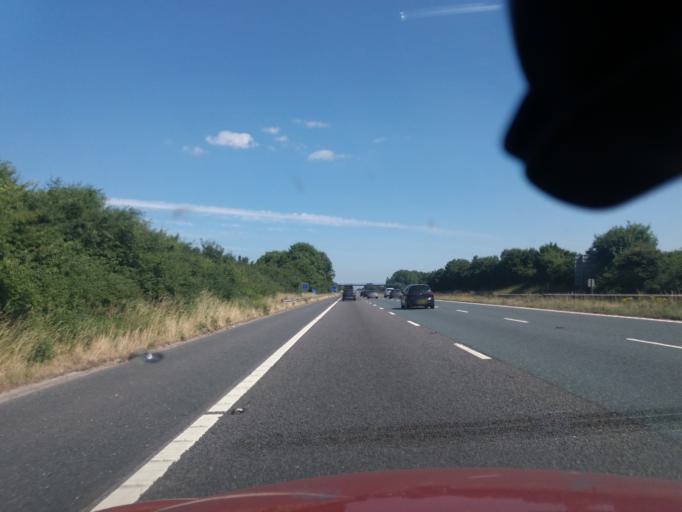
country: GB
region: England
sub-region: Borough of Wigan
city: Tyldesley
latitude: 53.5475
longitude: -2.4620
